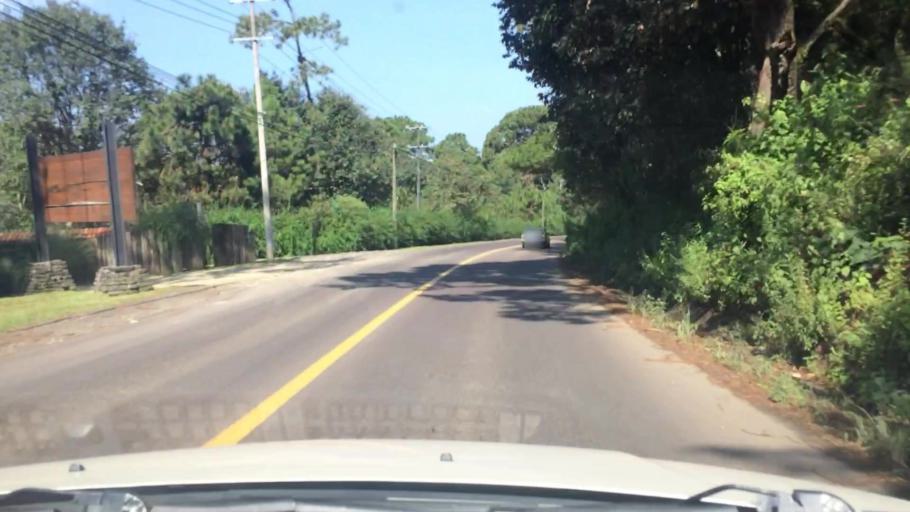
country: MX
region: Mexico
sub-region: Valle de Bravo
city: Casas Viejas
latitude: 19.1576
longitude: -100.0959
